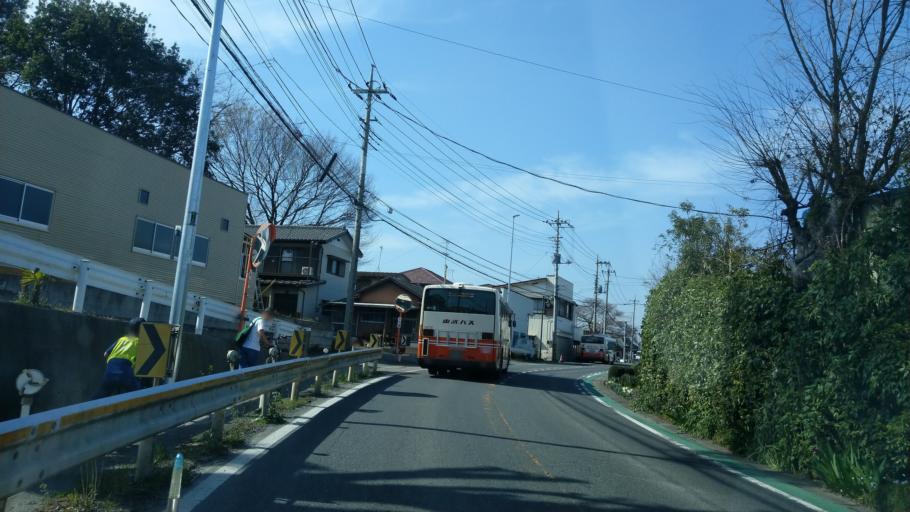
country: JP
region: Saitama
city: Okegawa
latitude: 35.9407
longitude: 139.5515
